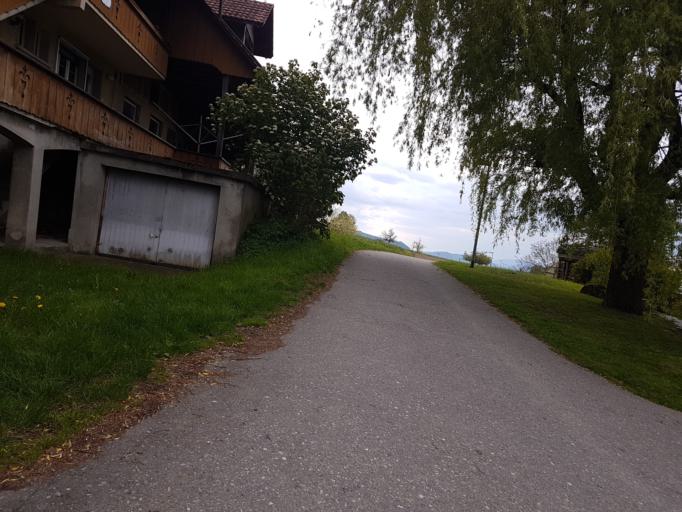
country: CH
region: Bern
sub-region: Seeland District
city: Arch
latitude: 47.1645
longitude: 7.4309
